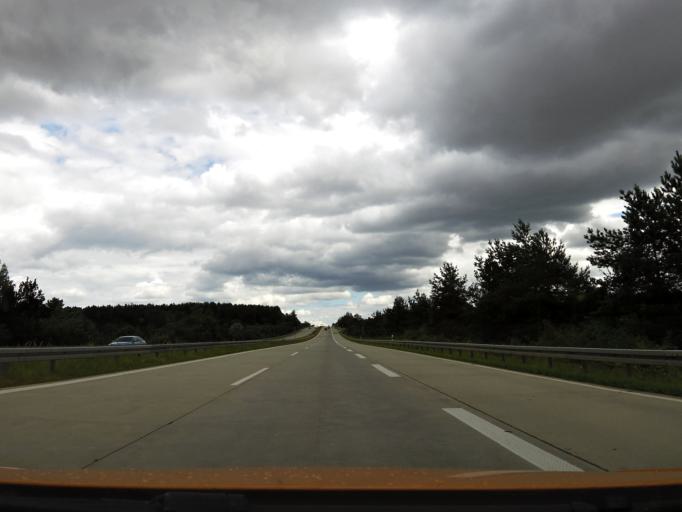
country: PL
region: West Pomeranian Voivodeship
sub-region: Powiat policki
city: Kolbaskowo
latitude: 53.3329
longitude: 14.3885
